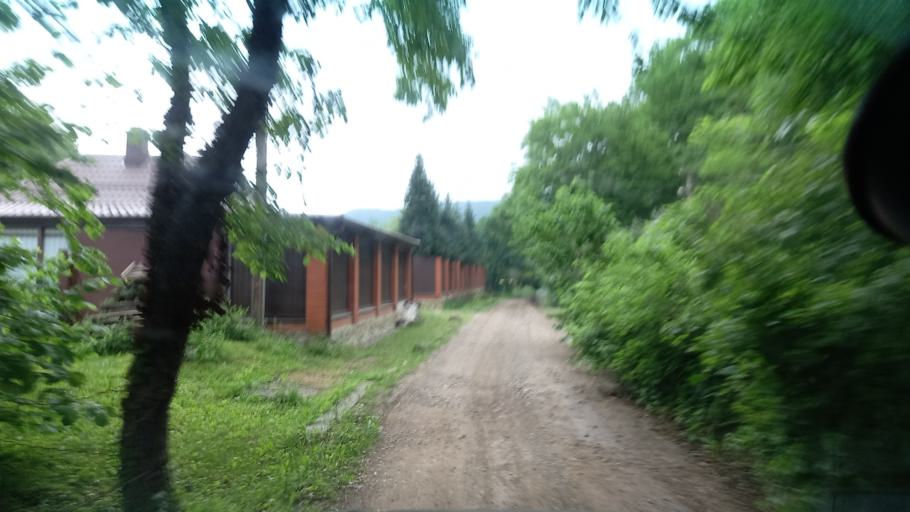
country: RU
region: Krasnodarskiy
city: Azovskaya
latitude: 44.6346
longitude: 38.6125
